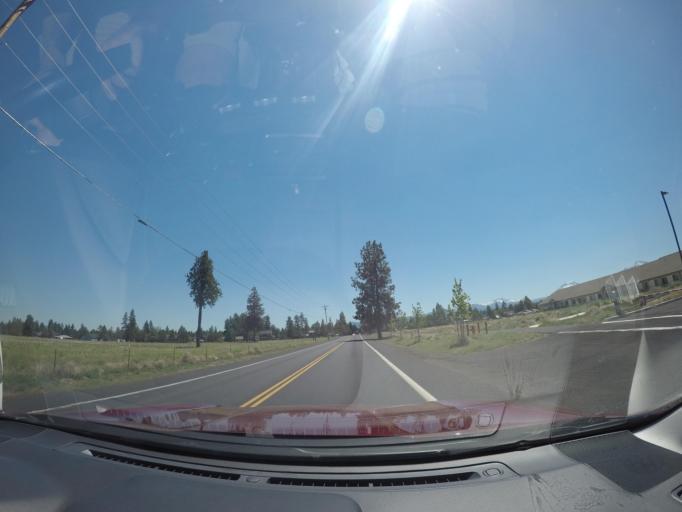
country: US
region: Oregon
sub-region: Deschutes County
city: Sisters
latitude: 44.2969
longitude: -121.5438
